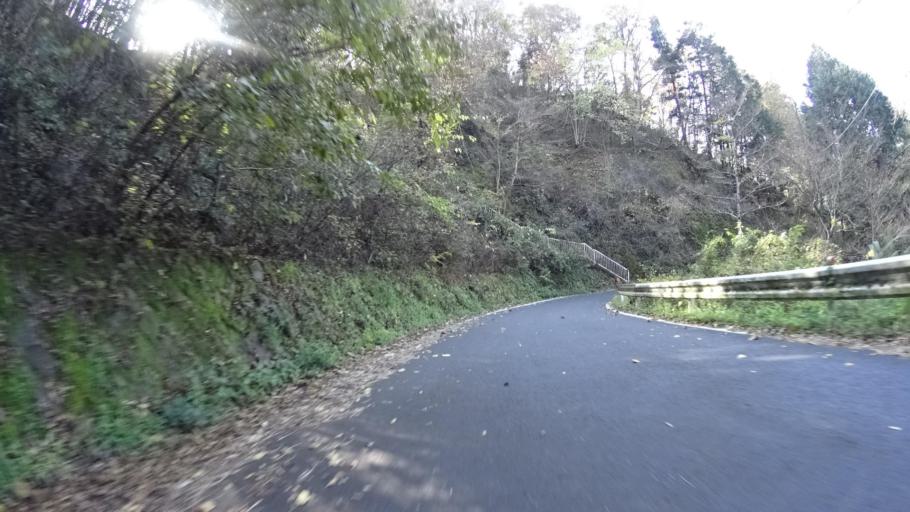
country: JP
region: Yamanashi
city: Uenohara
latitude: 35.5853
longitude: 139.1593
